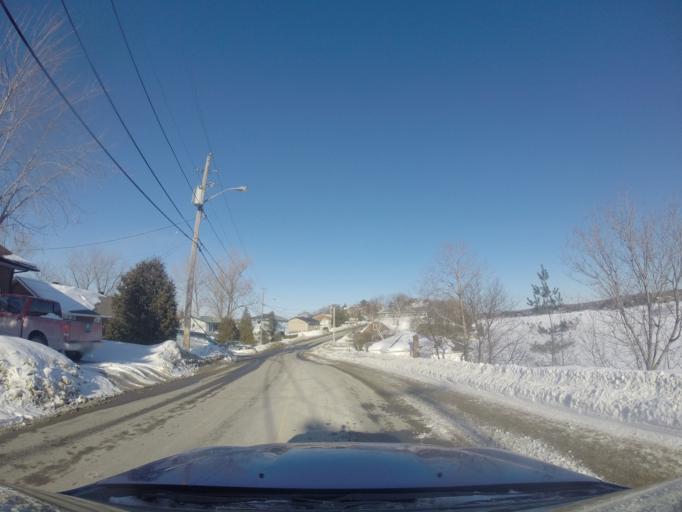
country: CA
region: Ontario
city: Greater Sudbury
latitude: 46.4561
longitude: -80.9980
